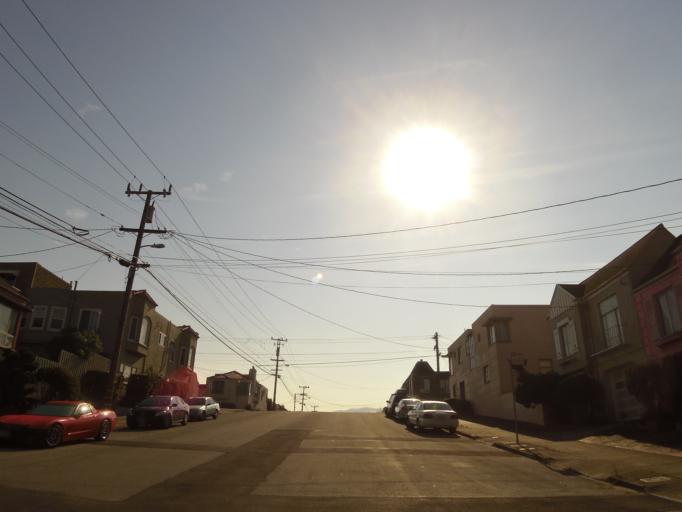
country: US
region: California
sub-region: San Mateo County
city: Daly City
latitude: 37.7572
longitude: -122.4922
